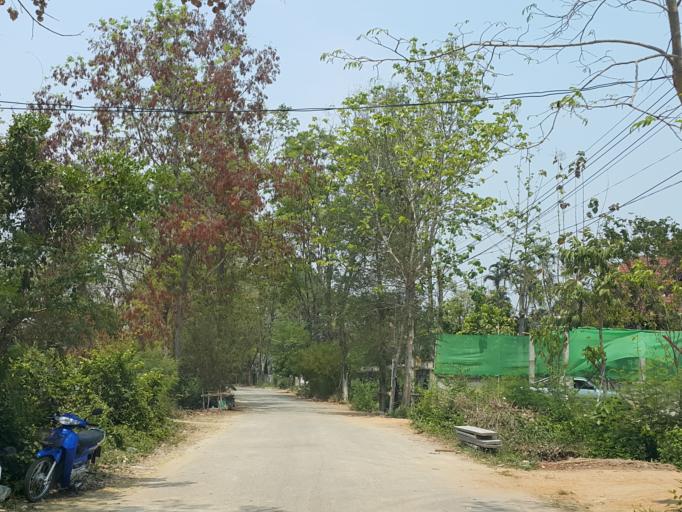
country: TH
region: Chiang Mai
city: Saraphi
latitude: 18.7285
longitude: 98.9774
